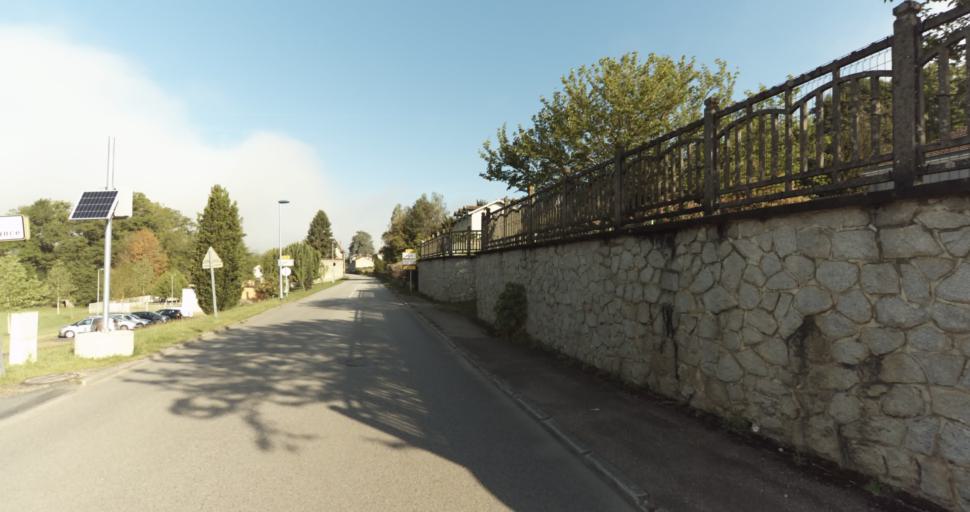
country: FR
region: Limousin
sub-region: Departement de la Haute-Vienne
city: Le Vigen
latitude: 45.7519
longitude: 1.2861
